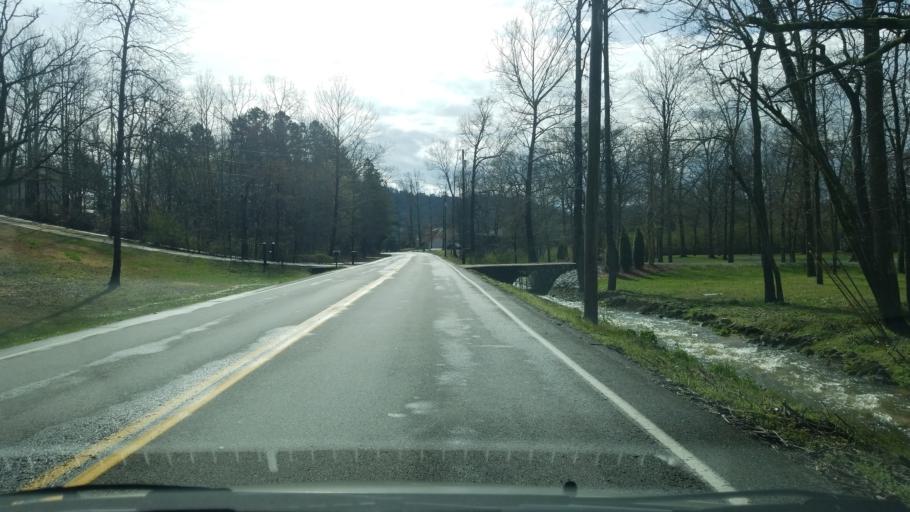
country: US
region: Tennessee
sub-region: Hamilton County
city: Collegedale
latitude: 35.0170
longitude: -85.0943
